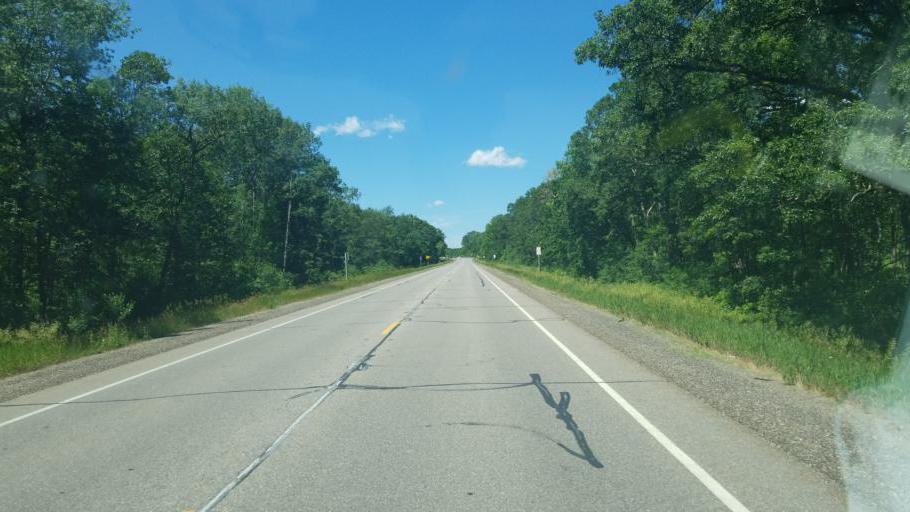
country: US
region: Wisconsin
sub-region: Adams County
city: Friendship
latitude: 44.0478
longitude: -90.0084
